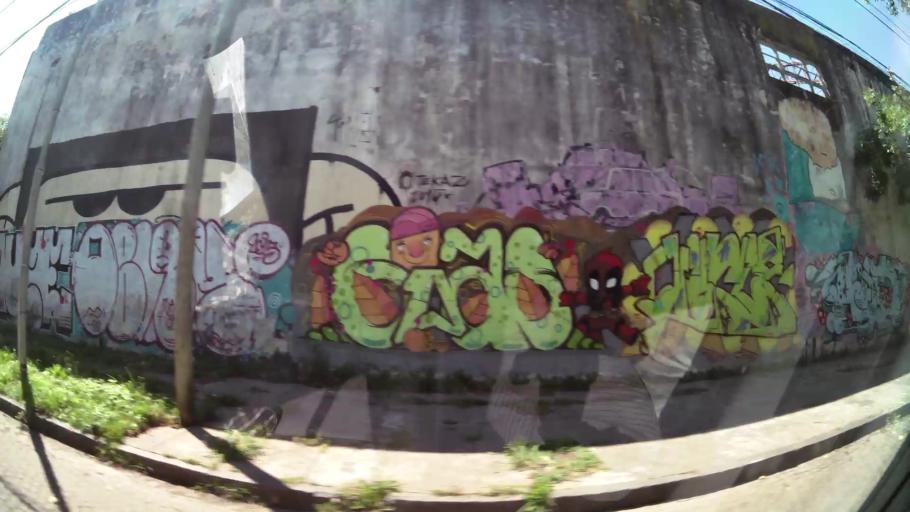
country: AR
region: Buenos Aires
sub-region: Partido de Tigre
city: Tigre
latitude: -34.4289
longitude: -58.5672
